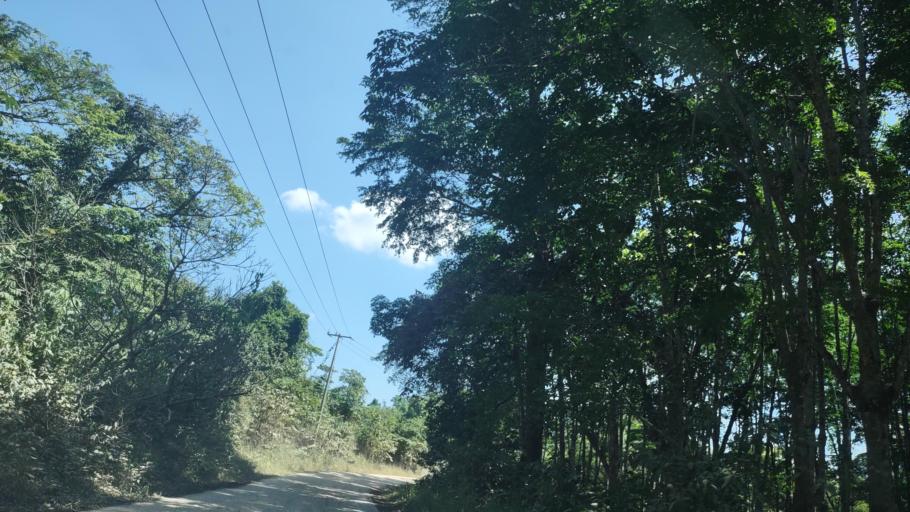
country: MX
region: Veracruz
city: Las Choapas
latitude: 17.7716
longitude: -94.1499
